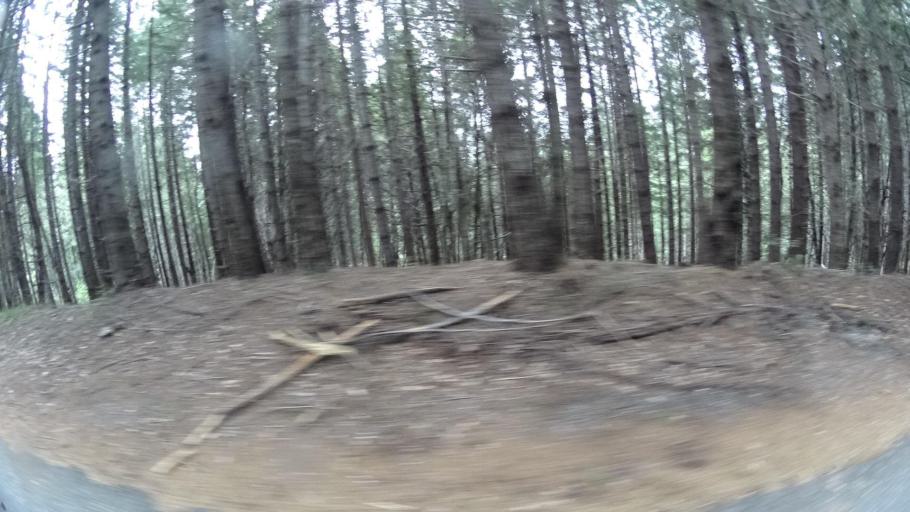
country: US
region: California
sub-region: Humboldt County
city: Willow Creek
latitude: 41.2014
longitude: -123.7798
